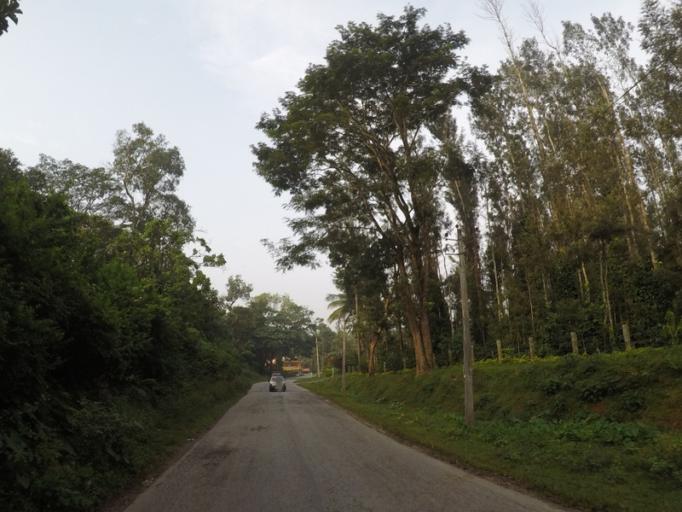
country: IN
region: Karnataka
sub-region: Chikmagalur
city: Chikmagalur
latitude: 13.2630
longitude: 75.6842
